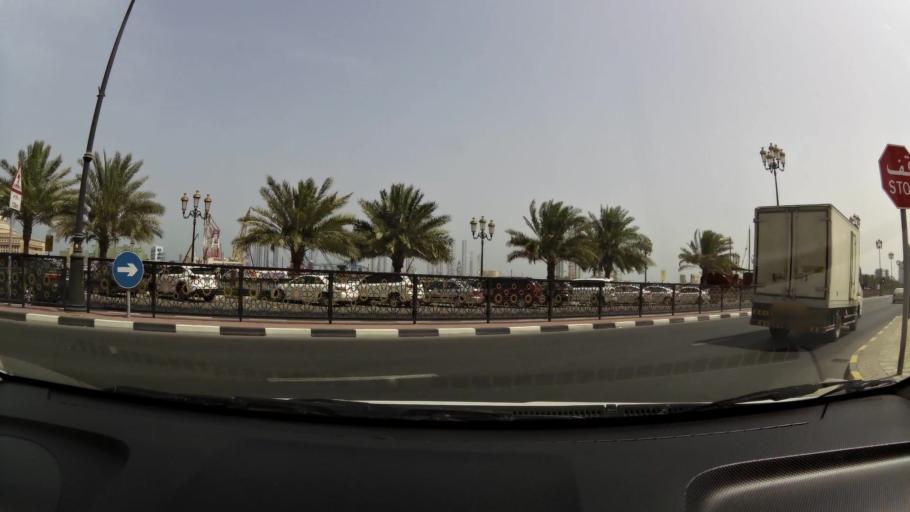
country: AE
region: Ash Shariqah
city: Sharjah
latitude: 25.3589
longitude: 55.3825
